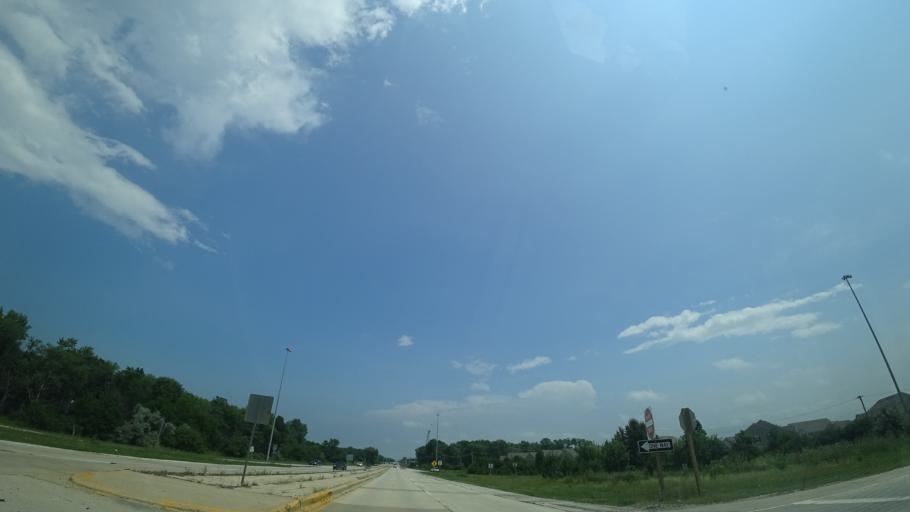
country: US
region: Illinois
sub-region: Cook County
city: Matteson
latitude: 41.5280
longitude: -87.7398
